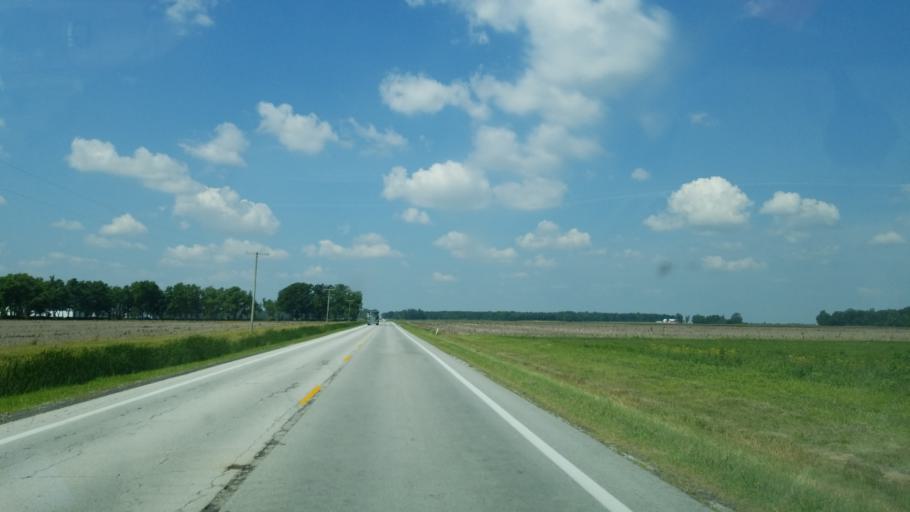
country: US
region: Ohio
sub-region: Wood County
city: Weston
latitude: 41.2838
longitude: -83.7122
